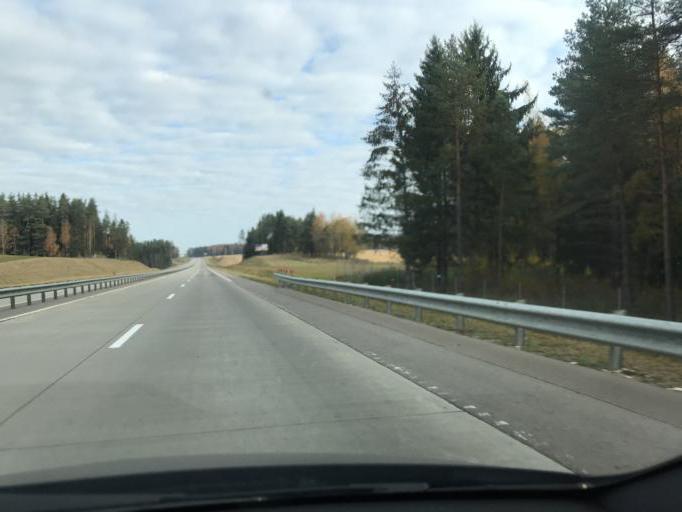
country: BY
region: Minsk
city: Rakaw
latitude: 53.9988
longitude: 27.1203
